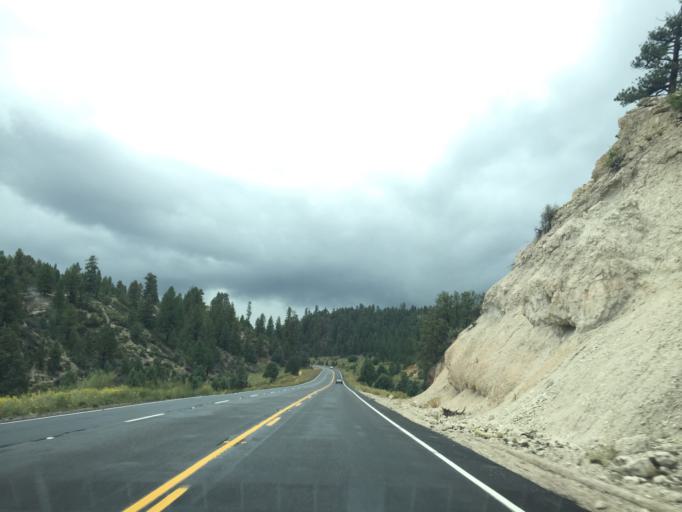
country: US
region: Utah
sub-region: Garfield County
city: Panguitch
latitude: 37.4732
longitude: -112.5140
